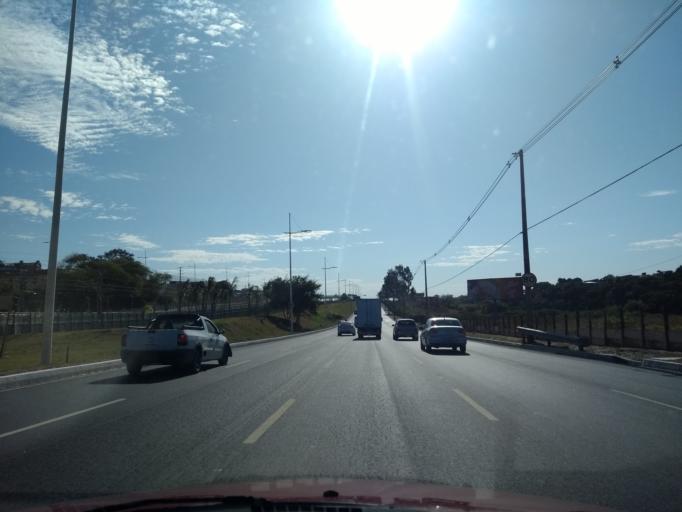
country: BR
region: Bahia
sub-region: Lauro De Freitas
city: Lauro de Freitas
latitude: -12.9235
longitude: -38.3713
